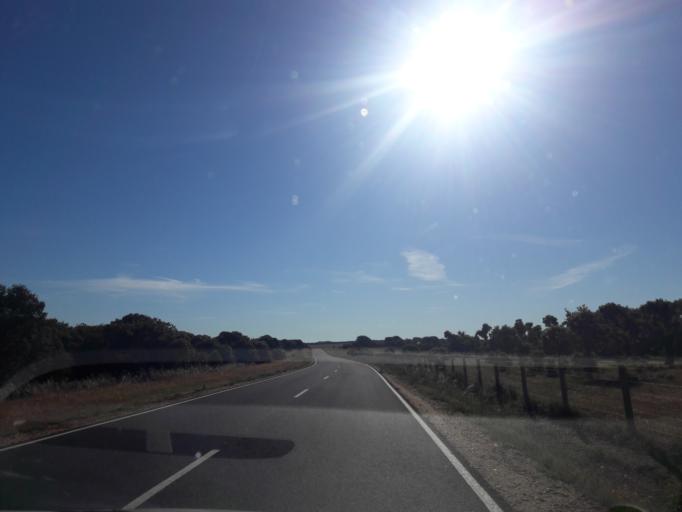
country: ES
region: Castille and Leon
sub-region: Provincia de Salamanca
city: Matilla de los Canos del Rio
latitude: 40.8384
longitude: -5.9000
